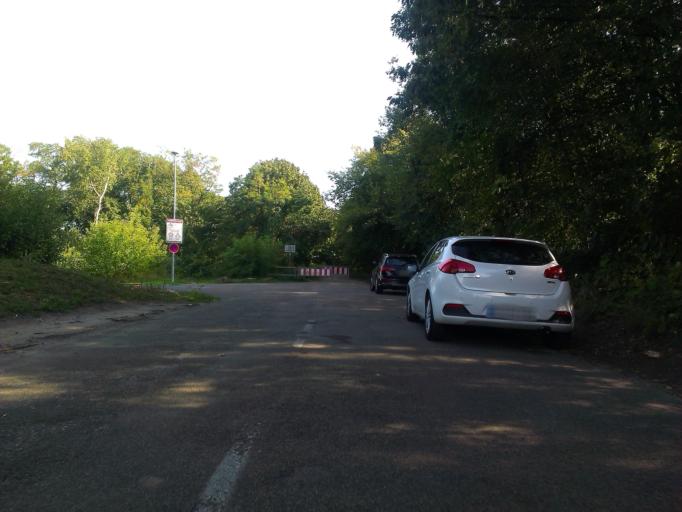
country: DE
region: Baden-Wuerttemberg
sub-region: Karlsruhe Region
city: Ilvesheim
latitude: 49.4443
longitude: 8.5599
